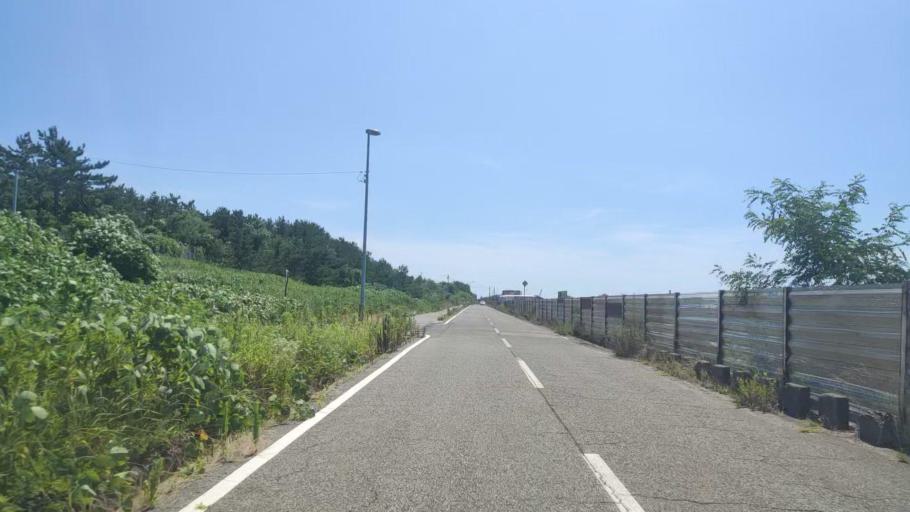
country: JP
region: Ishikawa
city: Kanazawa-shi
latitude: 36.6098
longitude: 136.5958
